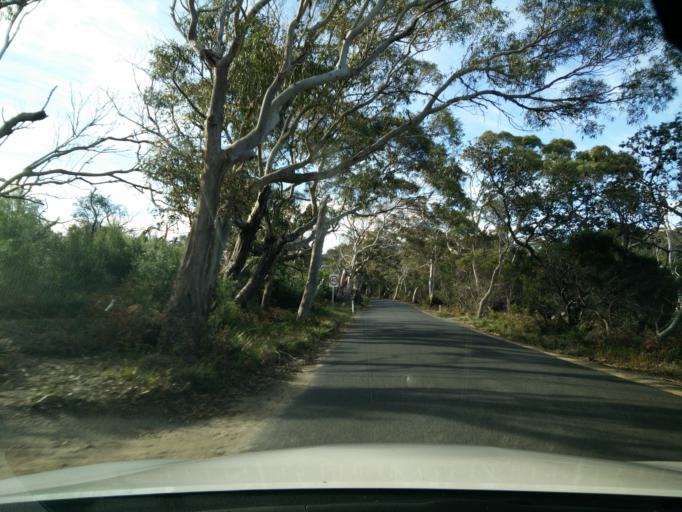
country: AU
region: Tasmania
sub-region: Break O'Day
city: St Helens
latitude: -42.1283
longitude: 148.3010
